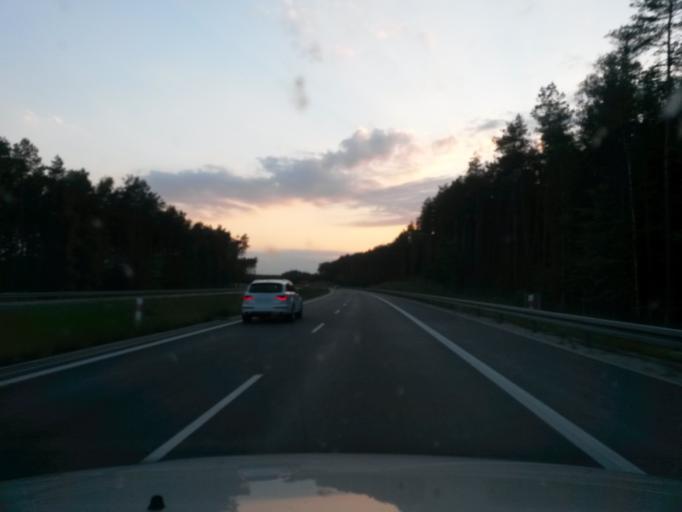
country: PL
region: Greater Poland Voivodeship
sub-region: Powiat kepinski
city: Perzow
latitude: 51.3033
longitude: 17.7951
